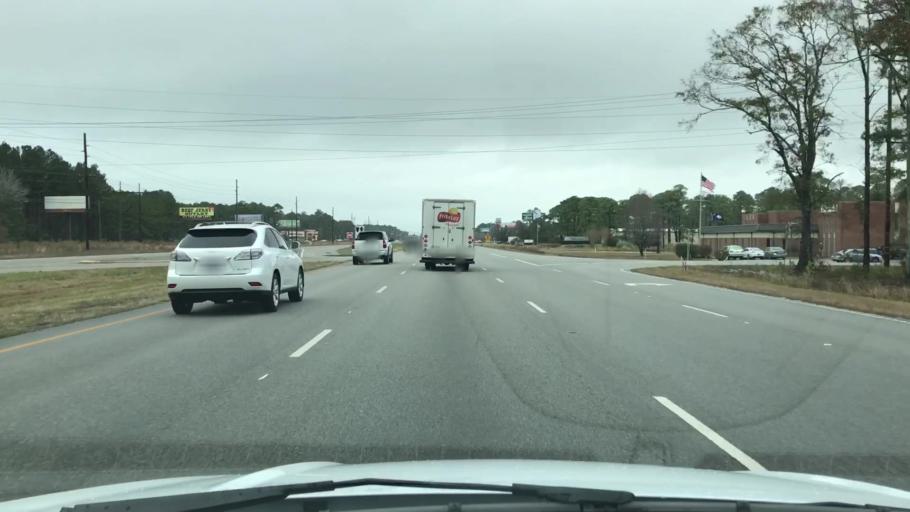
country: US
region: South Carolina
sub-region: Horry County
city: Forestbrook
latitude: 33.7714
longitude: -78.9793
